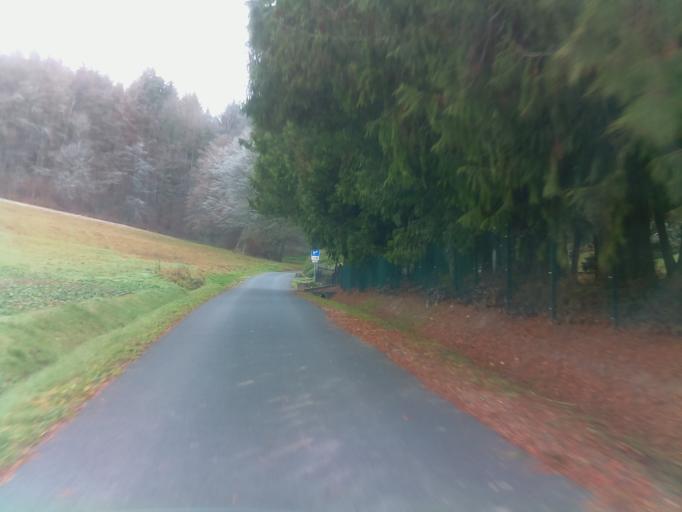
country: DE
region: Thuringia
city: Dorndorf
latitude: 50.8227
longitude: 10.1089
